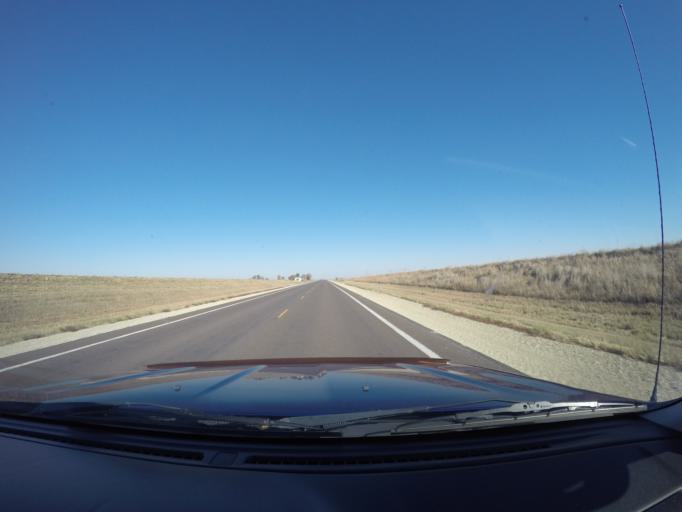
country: US
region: Kansas
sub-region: Marshall County
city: Blue Rapids
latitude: 39.6302
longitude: -96.7503
